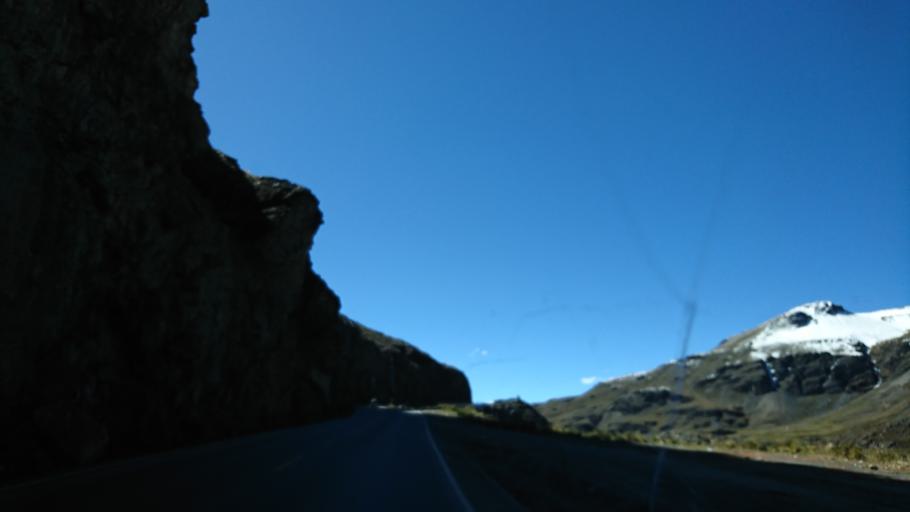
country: BO
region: La Paz
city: La Paz
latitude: -16.3870
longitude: -68.0426
